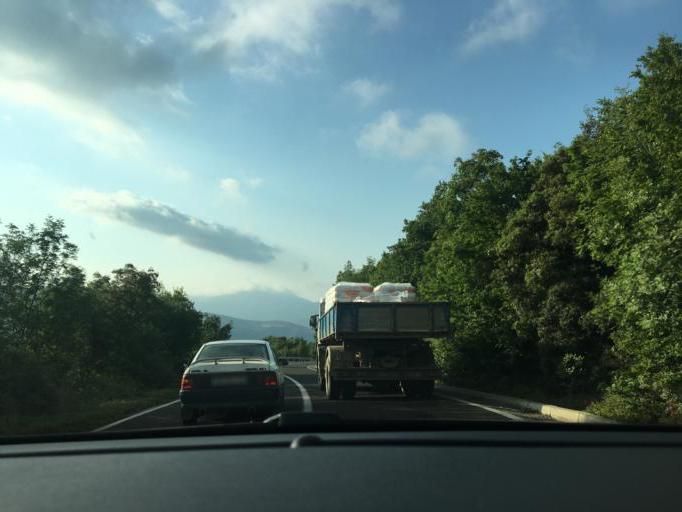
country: MK
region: Valandovo
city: Valandovo
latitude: 41.3367
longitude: 22.5886
